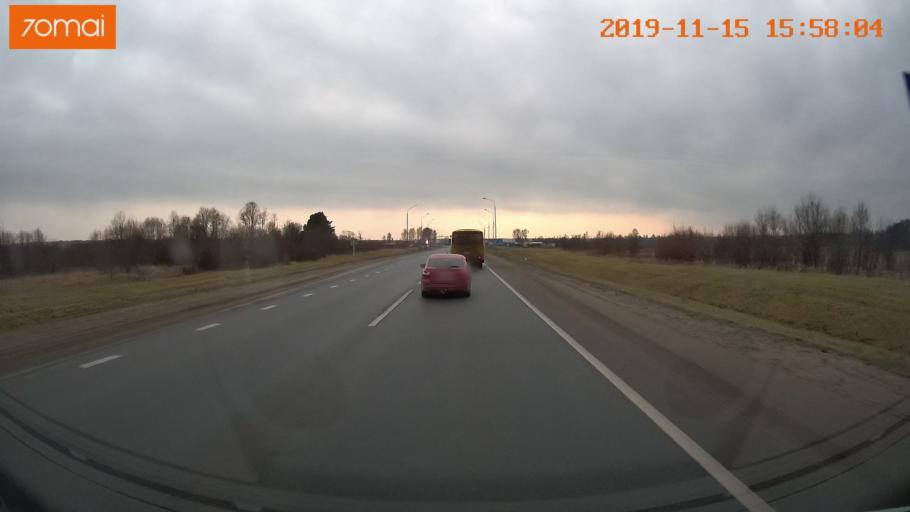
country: RU
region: Jaroslavl
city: Yaroslavl
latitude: 57.8240
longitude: 39.9580
